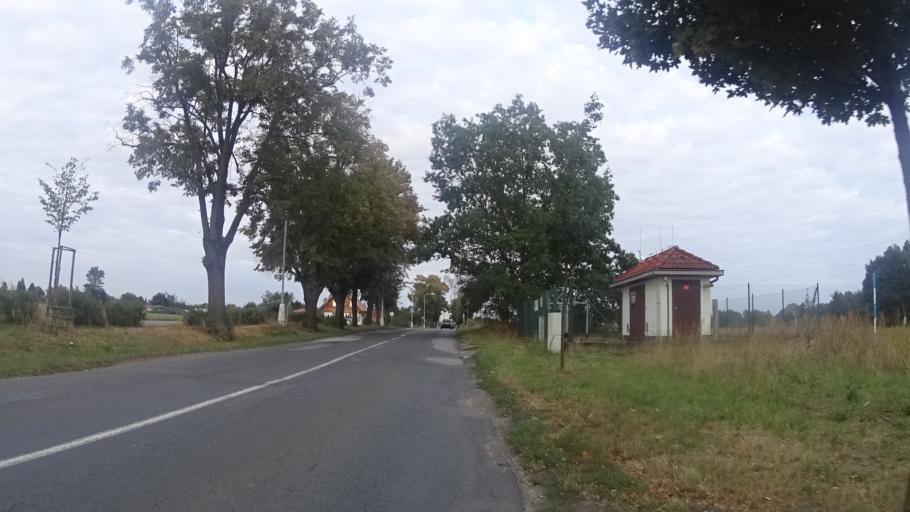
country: CZ
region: Kralovehradecky
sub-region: Okres Hradec Kralove
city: Hradec Kralove
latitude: 50.2067
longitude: 15.8699
